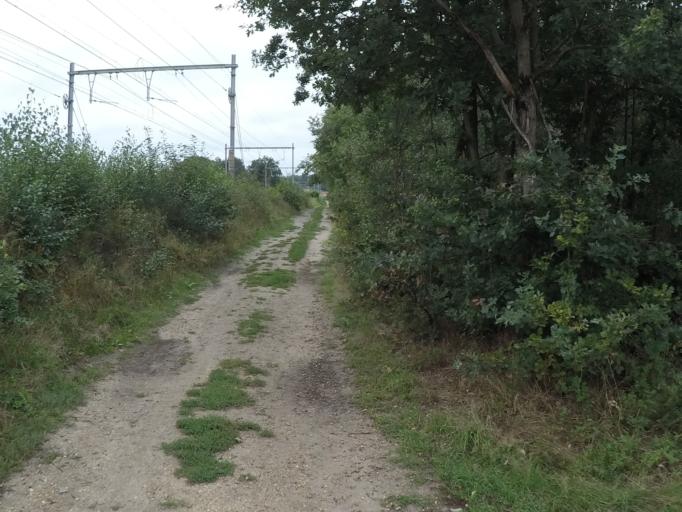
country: BE
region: Flanders
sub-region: Provincie Antwerpen
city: Herentals
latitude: 51.1868
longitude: 4.8507
